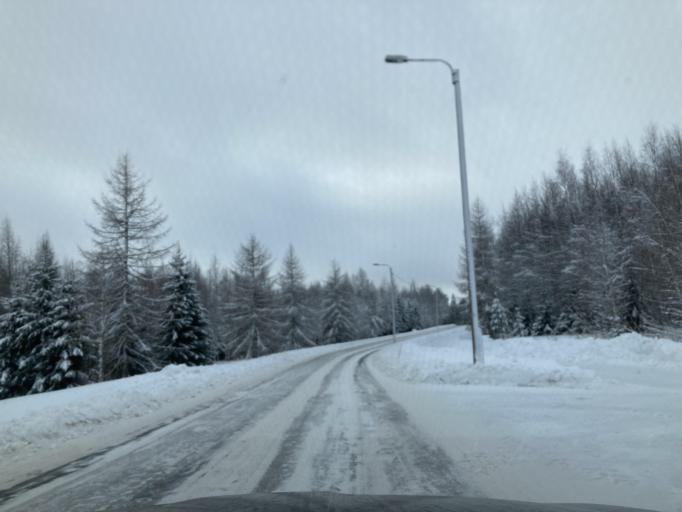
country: FI
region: Central Finland
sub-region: Jaemsae
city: Jaemsae
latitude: 61.8641
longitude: 25.2383
